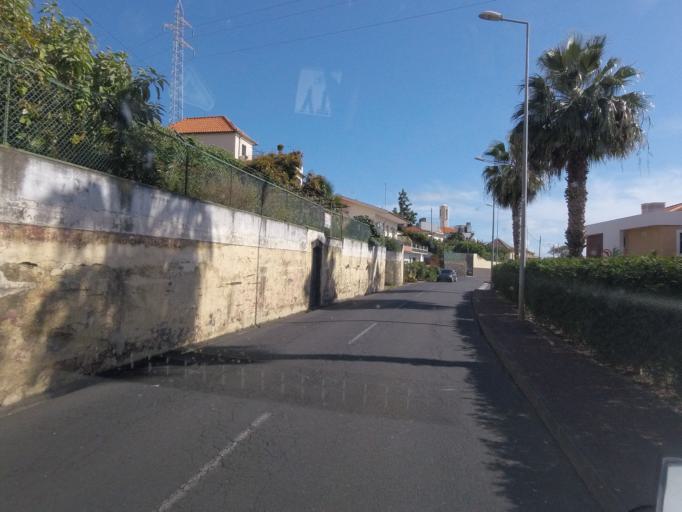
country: PT
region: Madeira
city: Camara de Lobos
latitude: 32.6552
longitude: -16.9705
